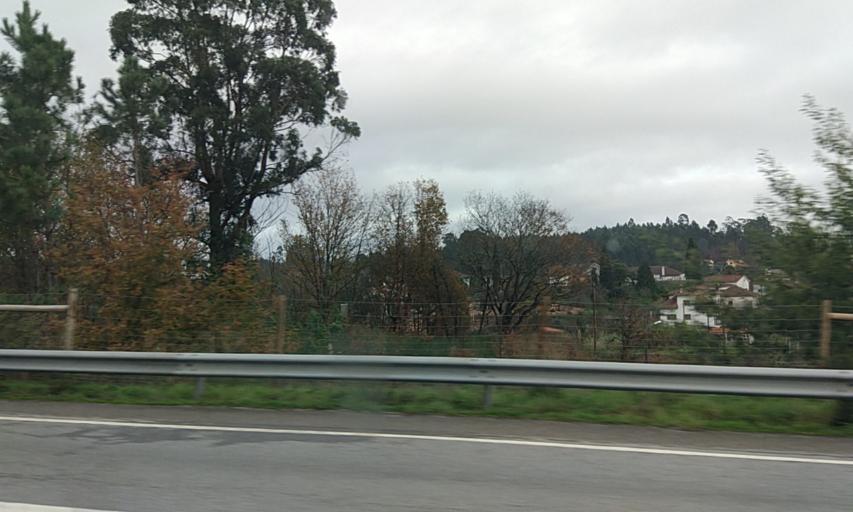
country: PT
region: Viseu
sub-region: Santa Comba Dao
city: Santa Comba Dao
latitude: 40.4181
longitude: -8.1210
